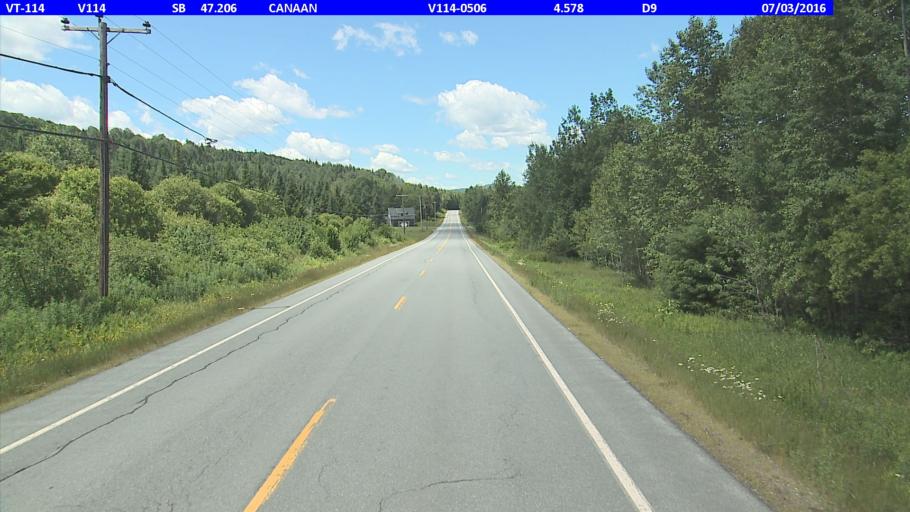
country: US
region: New Hampshire
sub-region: Coos County
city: Colebrook
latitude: 45.0073
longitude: -71.6027
